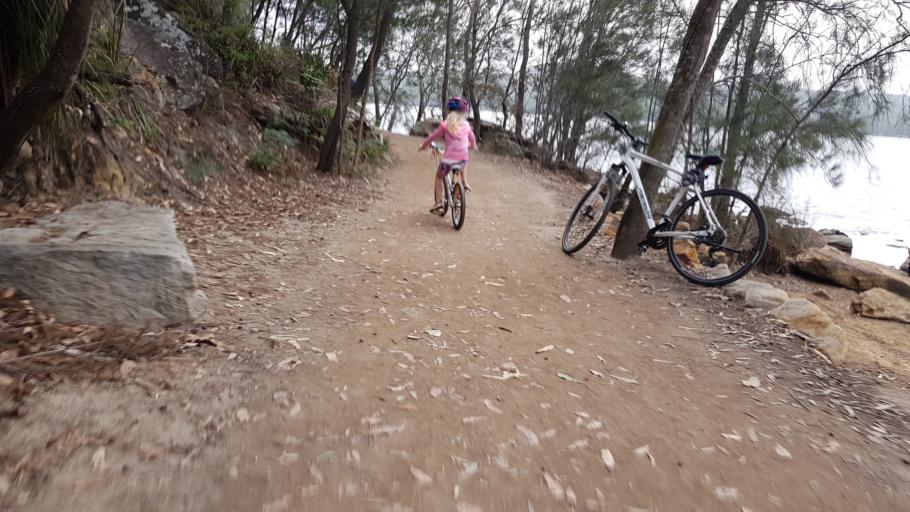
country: AU
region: New South Wales
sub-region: Pittwater
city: North Narrabeen
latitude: -33.7144
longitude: 151.2813
